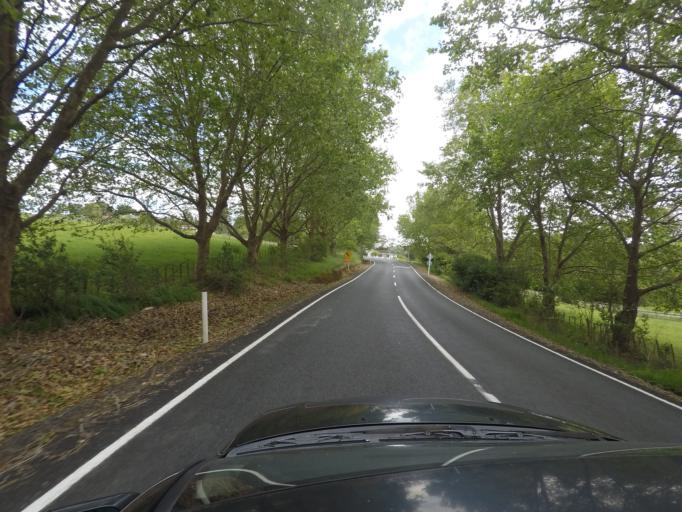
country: NZ
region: Auckland
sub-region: Auckland
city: Warkworth
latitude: -36.4836
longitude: 174.5324
